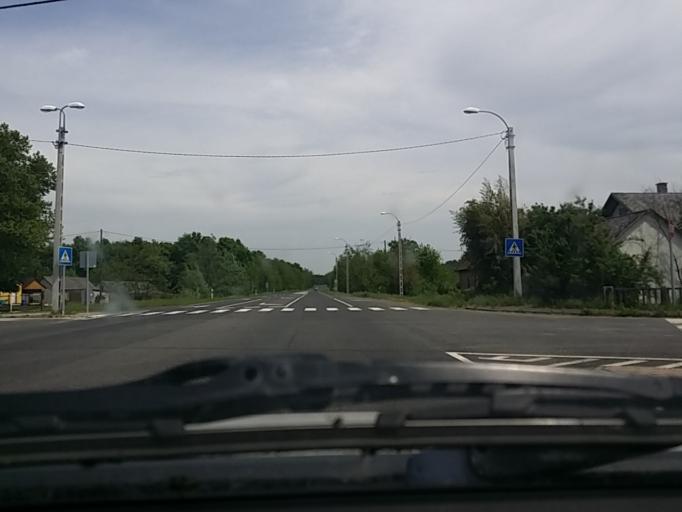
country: HU
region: Somogy
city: Barcs
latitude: 45.9584
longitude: 17.4855
